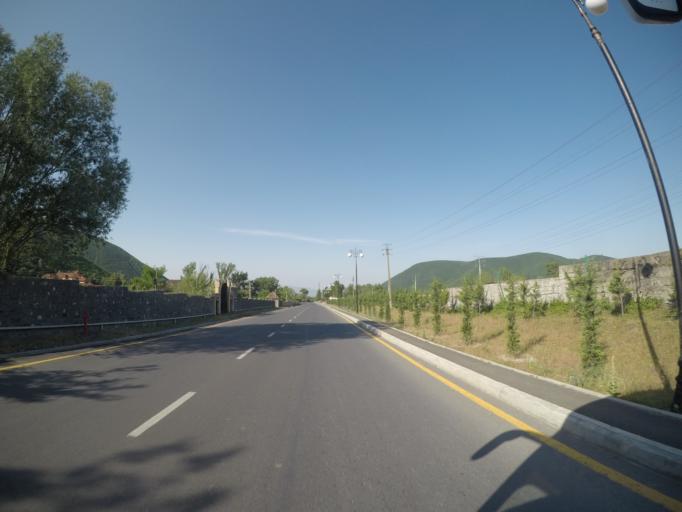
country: AZ
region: Shaki City
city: Sheki
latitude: 41.2357
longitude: 47.1809
